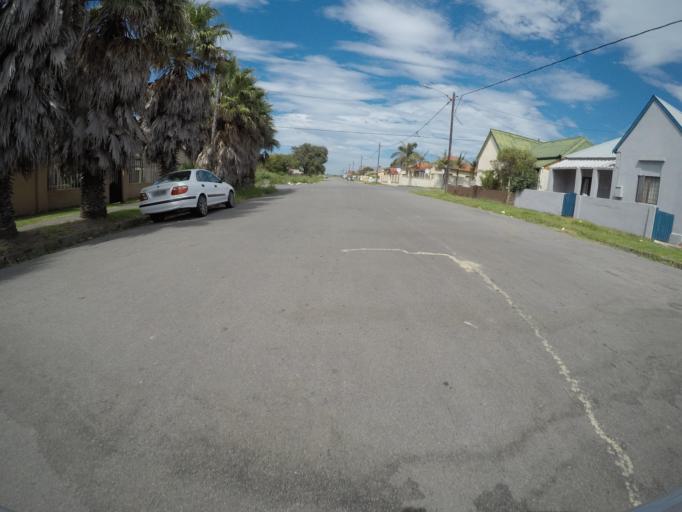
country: ZA
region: Eastern Cape
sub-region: Buffalo City Metropolitan Municipality
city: East London
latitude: -33.0360
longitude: 27.9058
